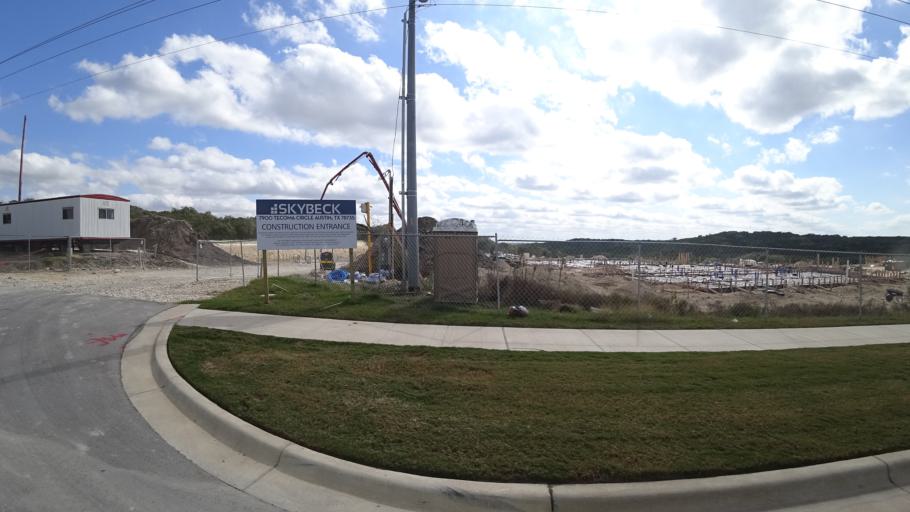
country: US
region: Texas
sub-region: Travis County
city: Barton Creek
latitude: 30.2616
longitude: -97.8568
